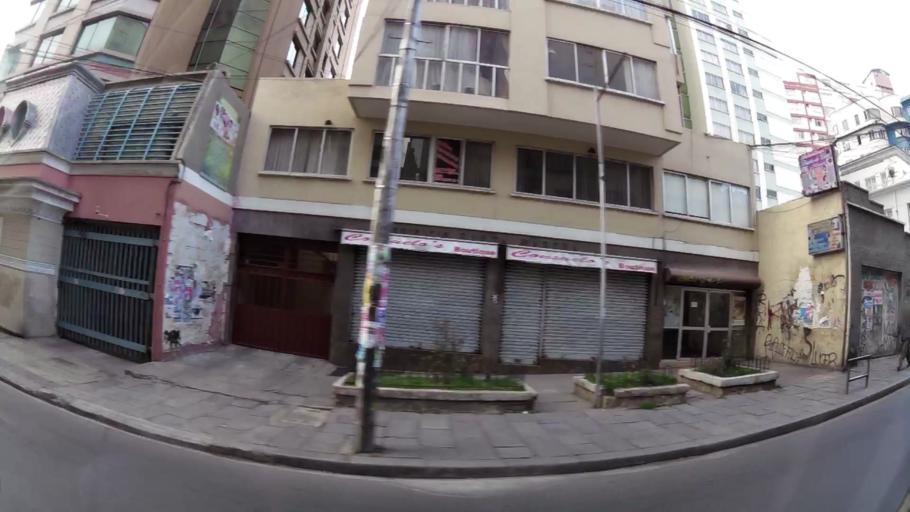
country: BO
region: La Paz
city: La Paz
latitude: -16.5105
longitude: -68.1256
